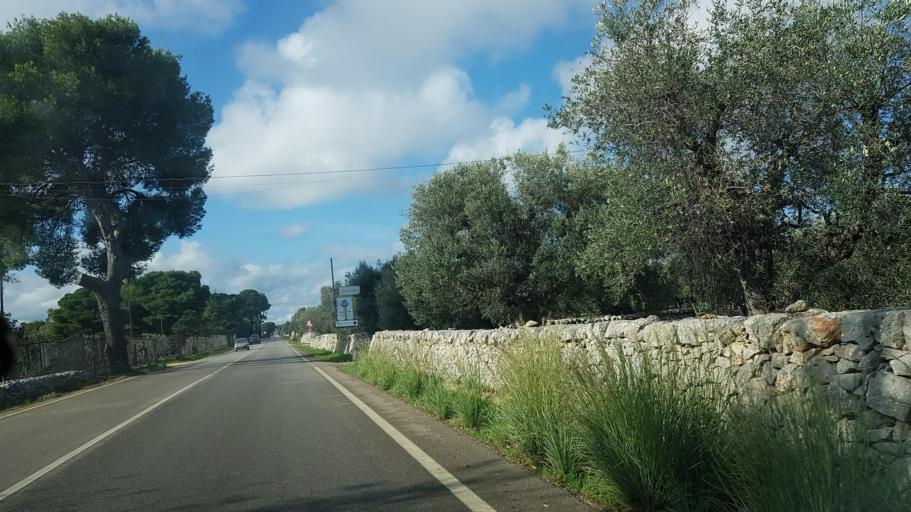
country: IT
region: Apulia
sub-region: Provincia di Brindisi
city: Carovigno
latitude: 40.7104
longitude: 17.6372
